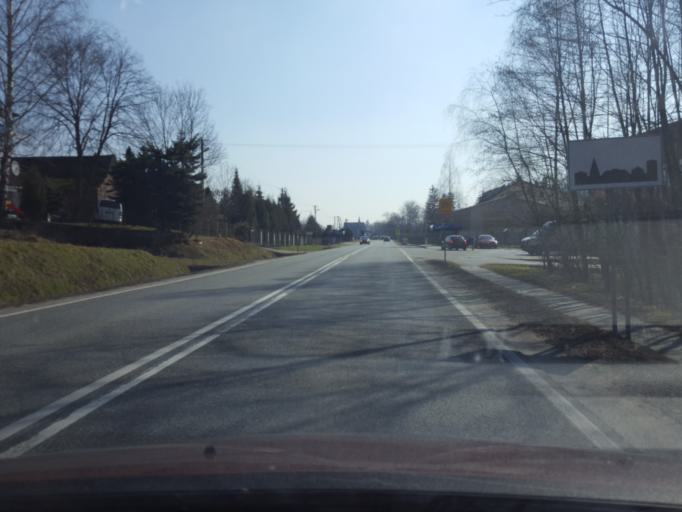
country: PL
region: Lesser Poland Voivodeship
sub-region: Powiat brzeski
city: Czchow
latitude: 49.8534
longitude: 20.6566
